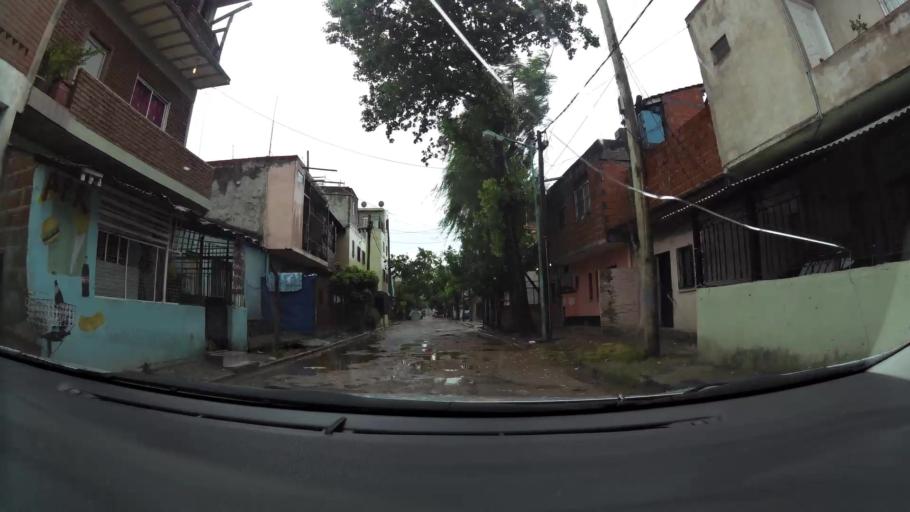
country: AR
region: Buenos Aires F.D.
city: Villa Lugano
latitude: -34.6578
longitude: -58.4579
